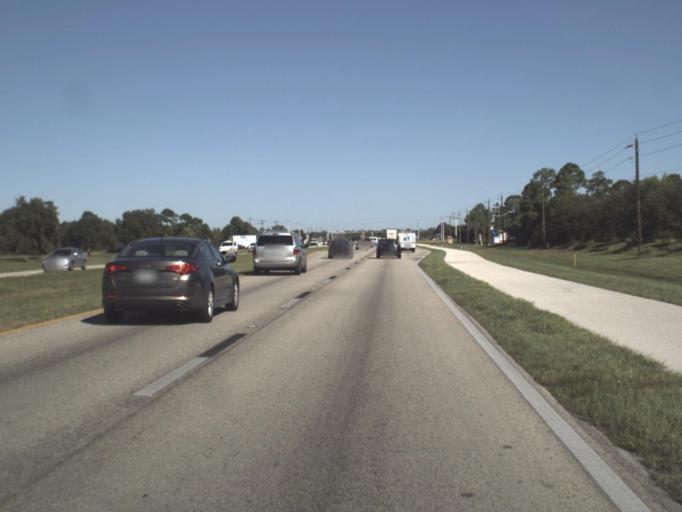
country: US
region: Florida
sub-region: Lee County
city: Villas
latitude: 26.5280
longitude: -81.8593
